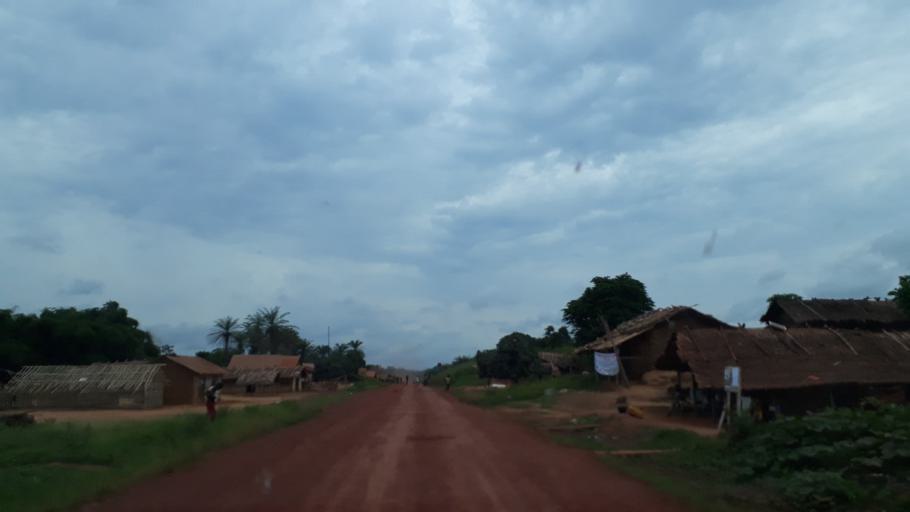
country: CD
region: Eastern Province
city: Kisangani
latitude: 0.6266
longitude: 26.0408
